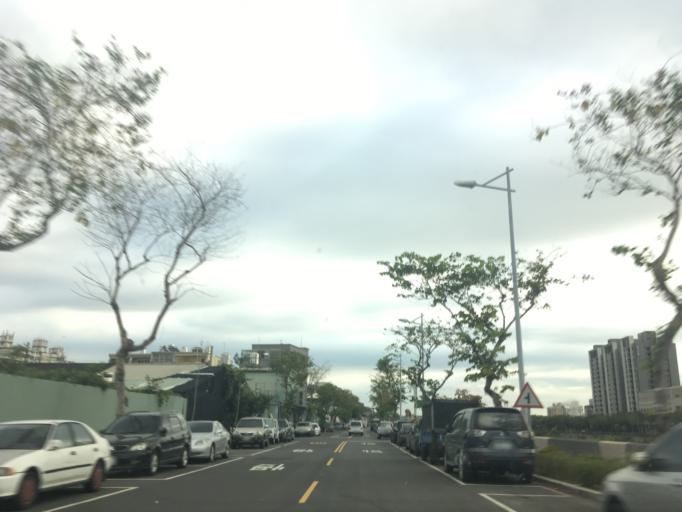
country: TW
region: Taiwan
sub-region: Taichung City
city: Taichung
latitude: 24.1563
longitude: 120.7282
